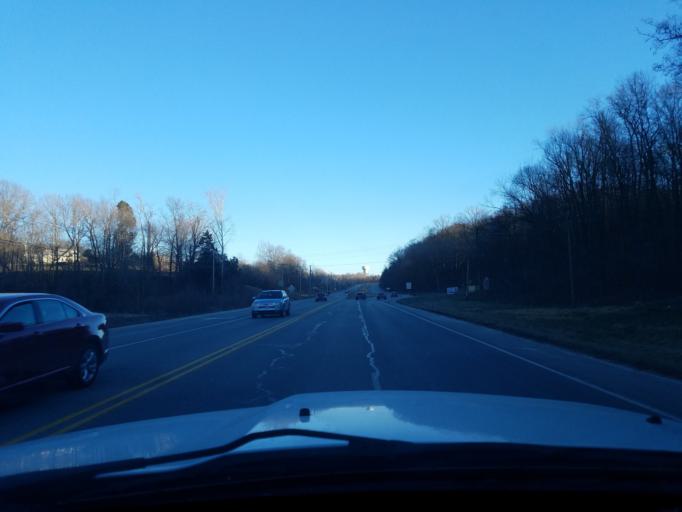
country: US
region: Indiana
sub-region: Floyd County
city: Galena
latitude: 38.3419
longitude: -85.9122
